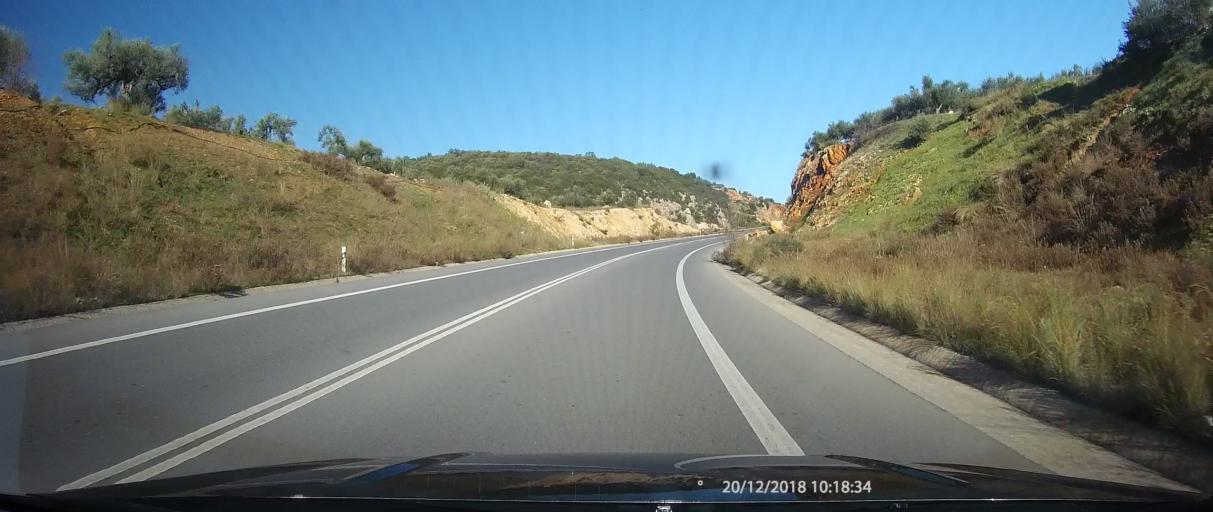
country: GR
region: Peloponnese
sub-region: Nomos Lakonias
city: Magoula
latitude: 37.1185
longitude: 22.4217
